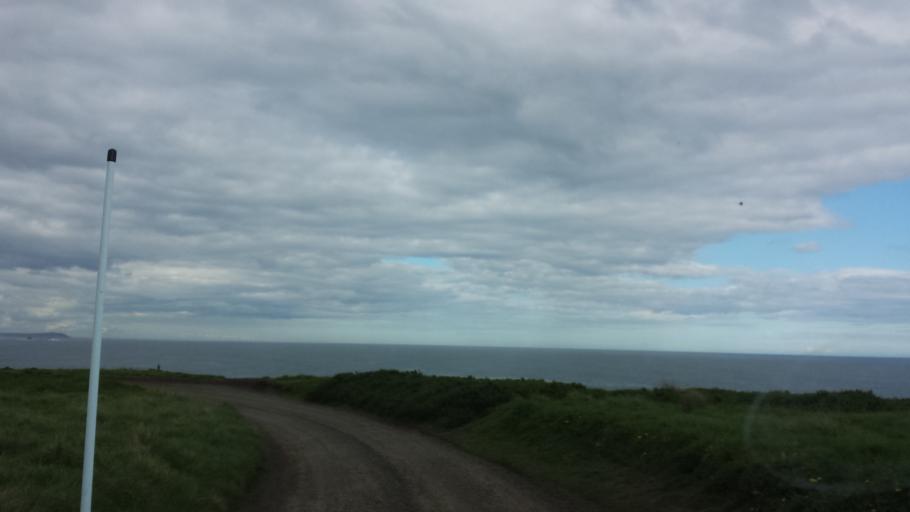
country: AU
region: Victoria
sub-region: Bass Coast
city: Phillip Island
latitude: -38.5149
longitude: 145.1444
